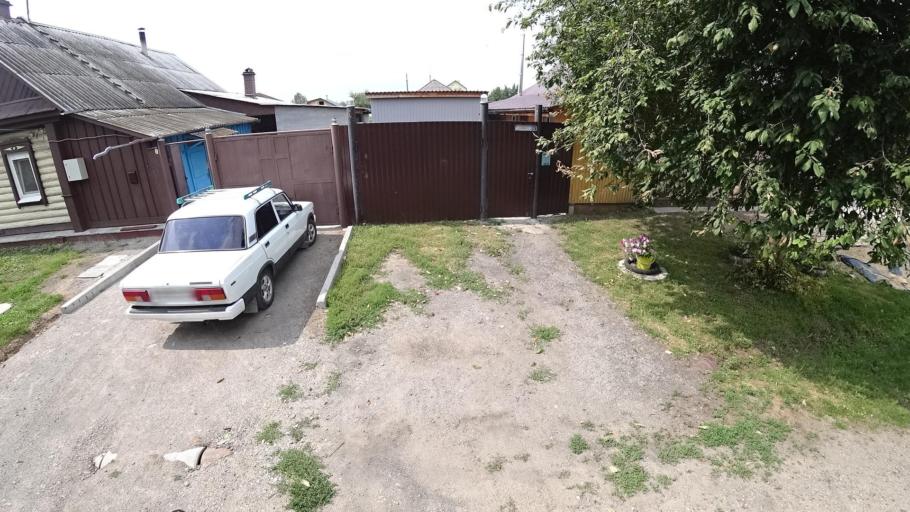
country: RU
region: Sverdlovsk
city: Kamyshlov
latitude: 56.8497
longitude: 62.6815
